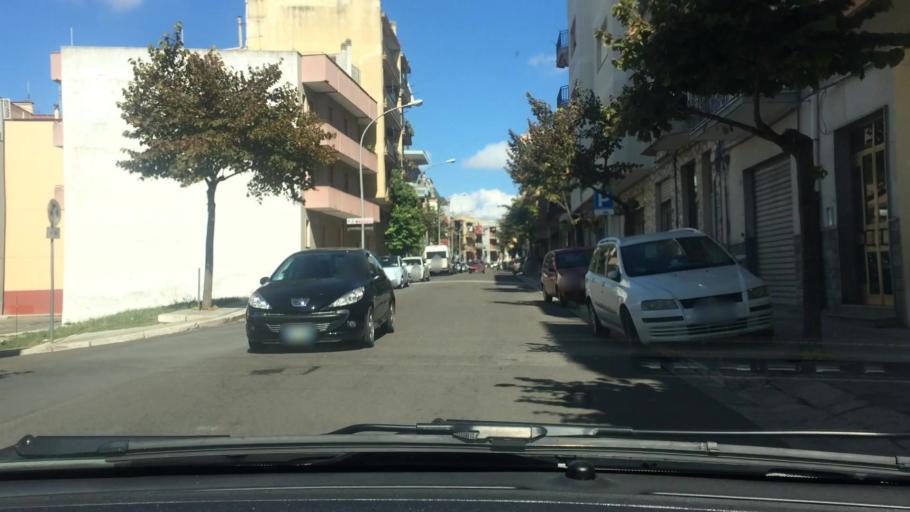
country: IT
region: Basilicate
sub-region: Provincia di Matera
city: Montescaglioso
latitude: 40.5481
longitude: 16.6669
